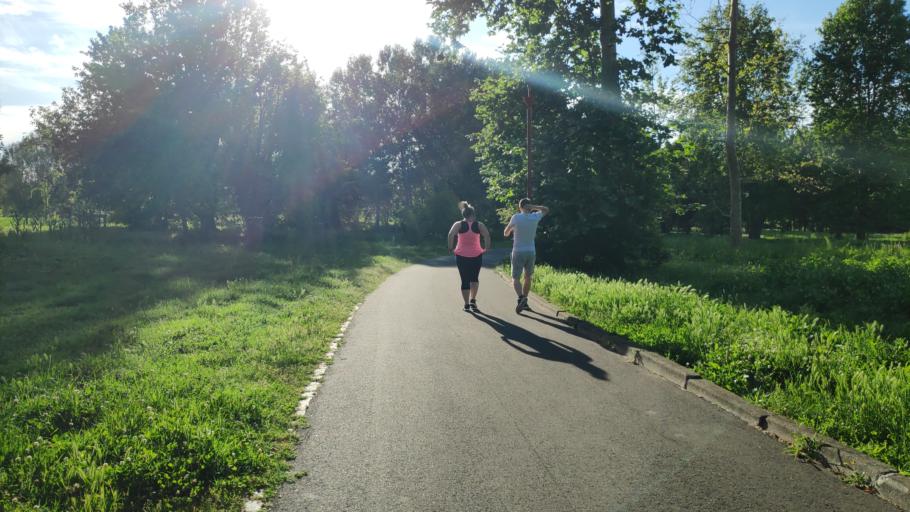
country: IT
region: Lombardy
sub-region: Citta metropolitana di Milano
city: Basiglio
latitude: 45.3546
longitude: 9.1586
